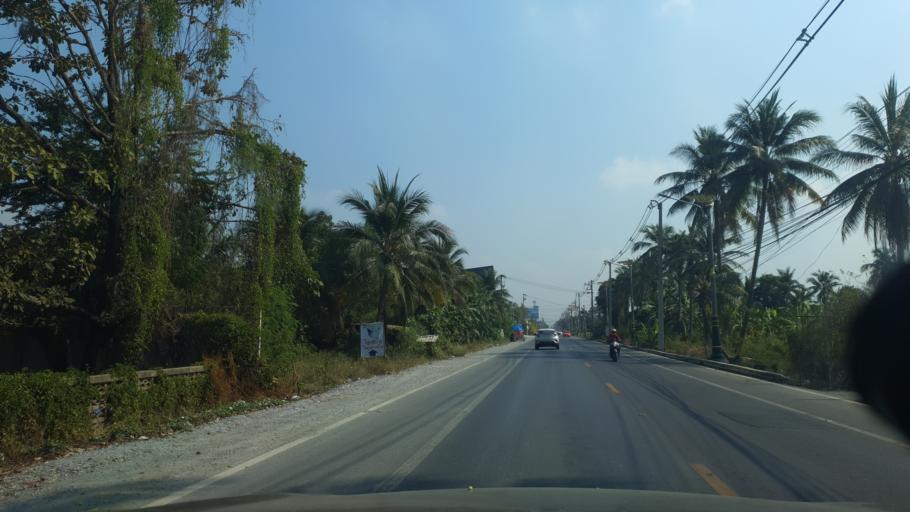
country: TH
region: Nakhon Pathom
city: Salaya
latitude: 13.7720
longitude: 100.2889
